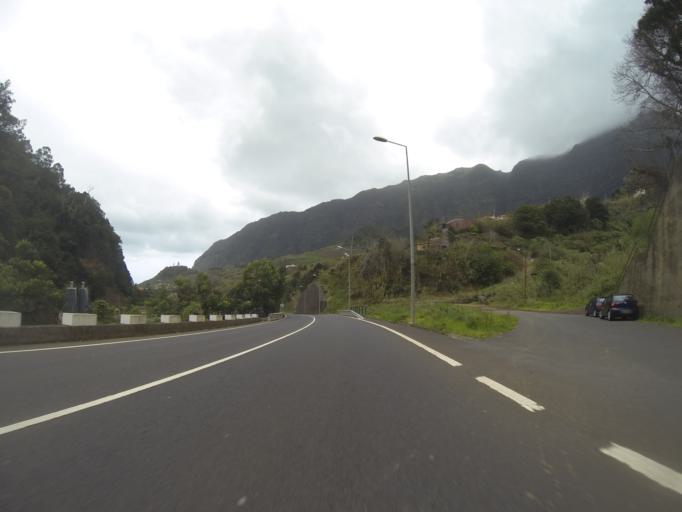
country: PT
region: Madeira
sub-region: Sao Vicente
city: Sao Vicente
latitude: 32.7887
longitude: -17.0301
